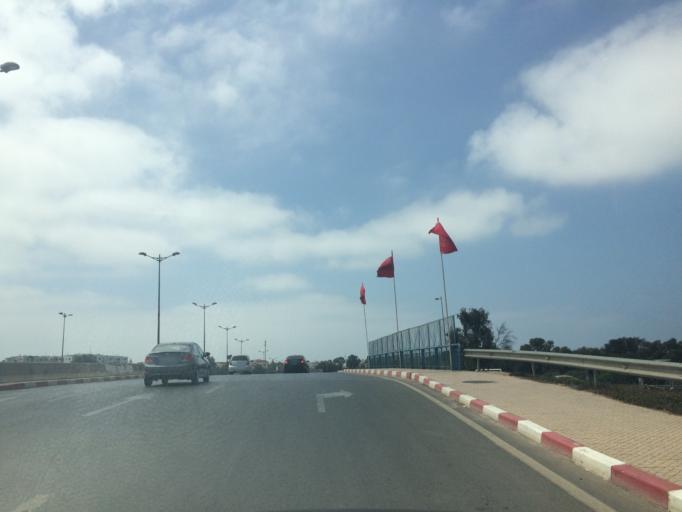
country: MA
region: Rabat-Sale-Zemmour-Zaer
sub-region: Skhirate-Temara
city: Temara
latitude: 33.9716
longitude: -6.8783
